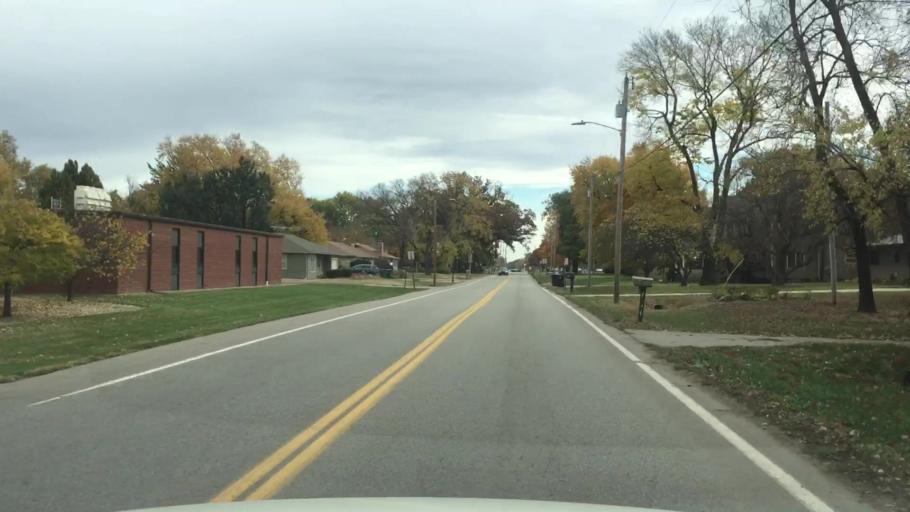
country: US
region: Kansas
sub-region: Shawnee County
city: Topeka
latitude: 39.0876
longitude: -95.6776
